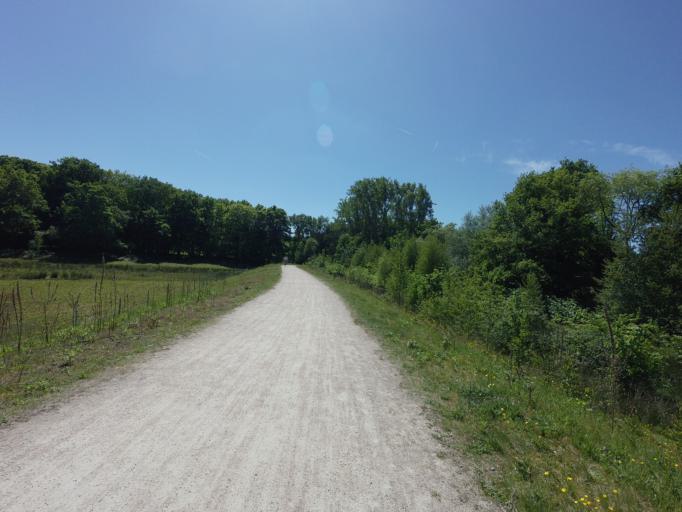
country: NL
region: North Holland
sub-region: Gemeente Hilversum
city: Hilversum
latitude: 52.2220
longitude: 5.2107
